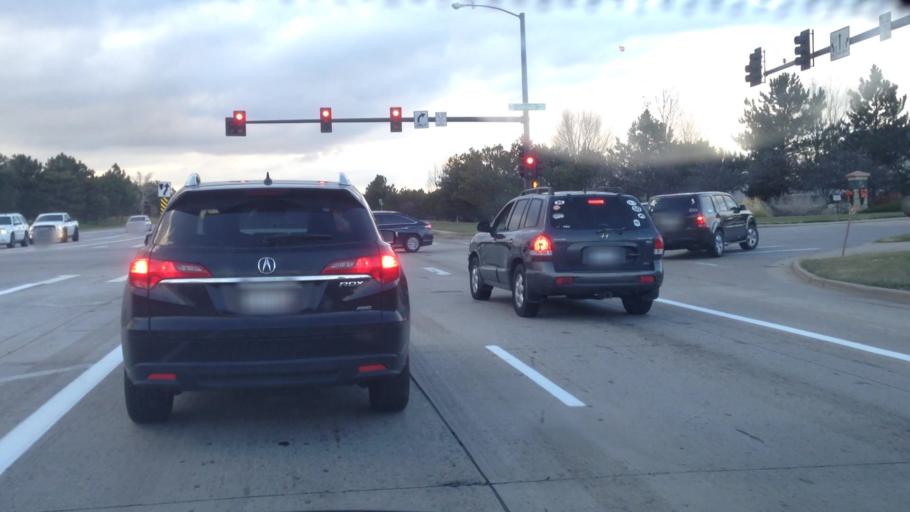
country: US
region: Colorado
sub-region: Douglas County
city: Stonegate
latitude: 39.5347
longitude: -104.8055
